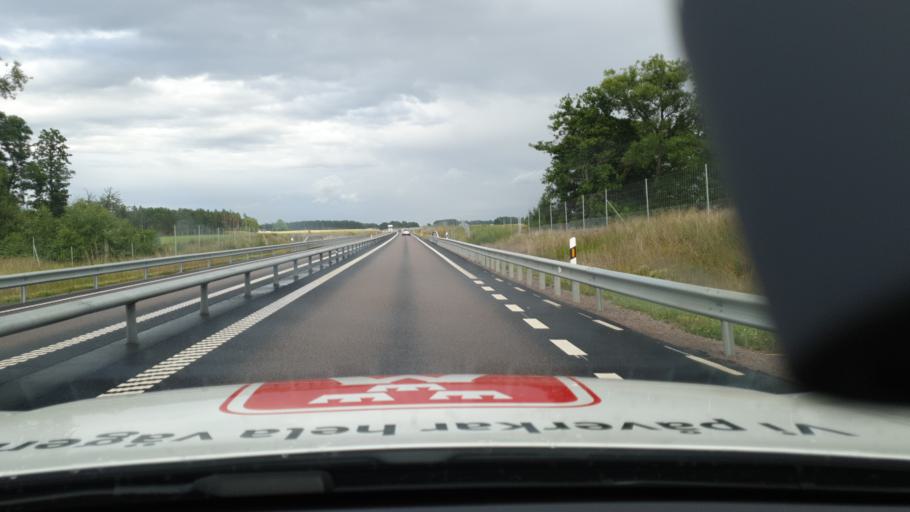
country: SE
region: Vaestra Goetaland
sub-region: Lidkopings Kommun
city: Vinninga
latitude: 58.4779
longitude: 13.2381
